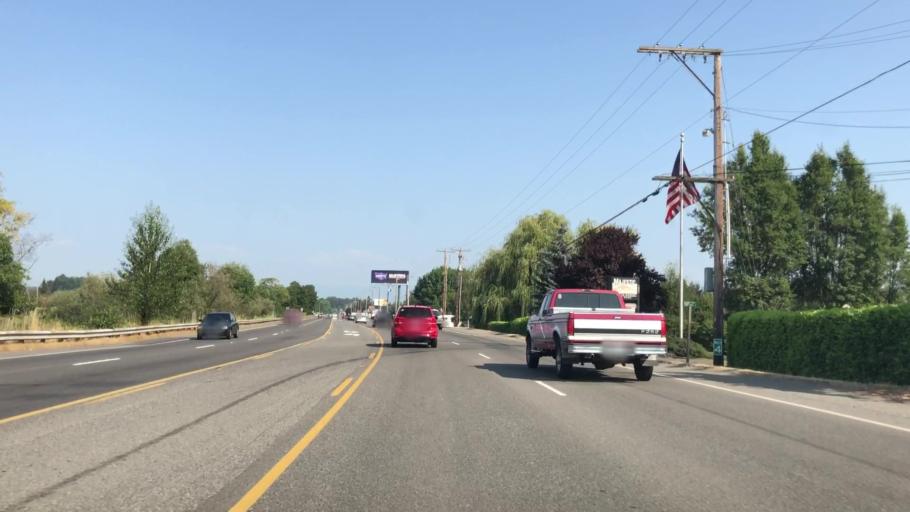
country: US
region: Washington
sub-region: Pierce County
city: Waller
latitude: 47.2108
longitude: -122.3366
